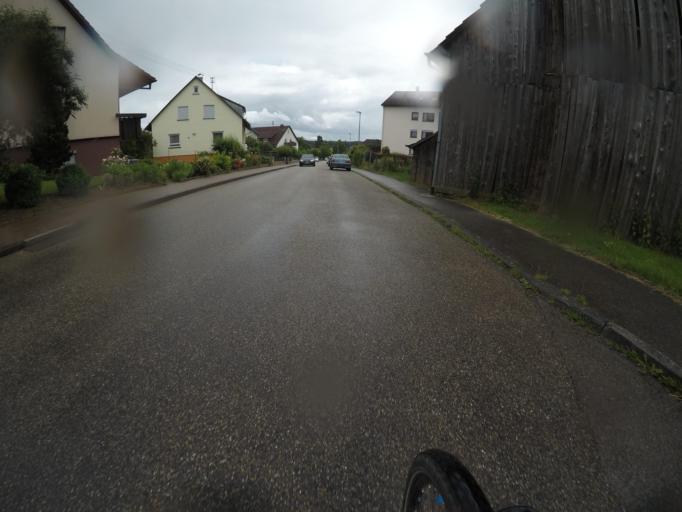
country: DE
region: Baden-Wuerttemberg
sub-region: Regierungsbezirk Stuttgart
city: Motzingen
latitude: 48.5313
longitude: 8.7798
